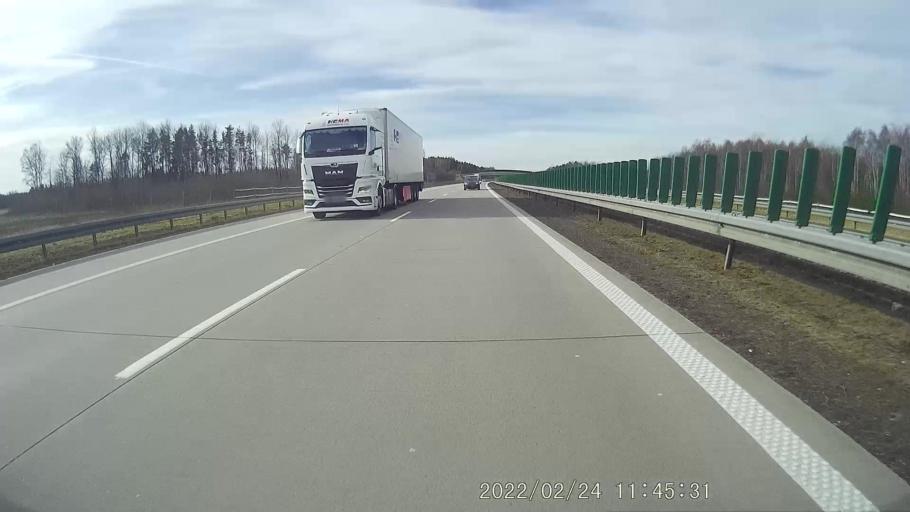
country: PL
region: Lower Silesian Voivodeship
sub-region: Powiat polkowicki
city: Radwanice
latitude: 51.5625
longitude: 15.9356
